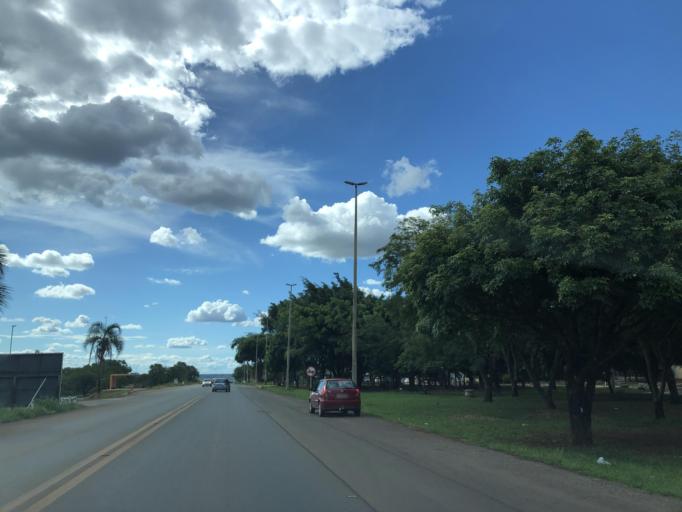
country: BR
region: Goias
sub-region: Luziania
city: Luziania
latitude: -16.0298
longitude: -48.0804
